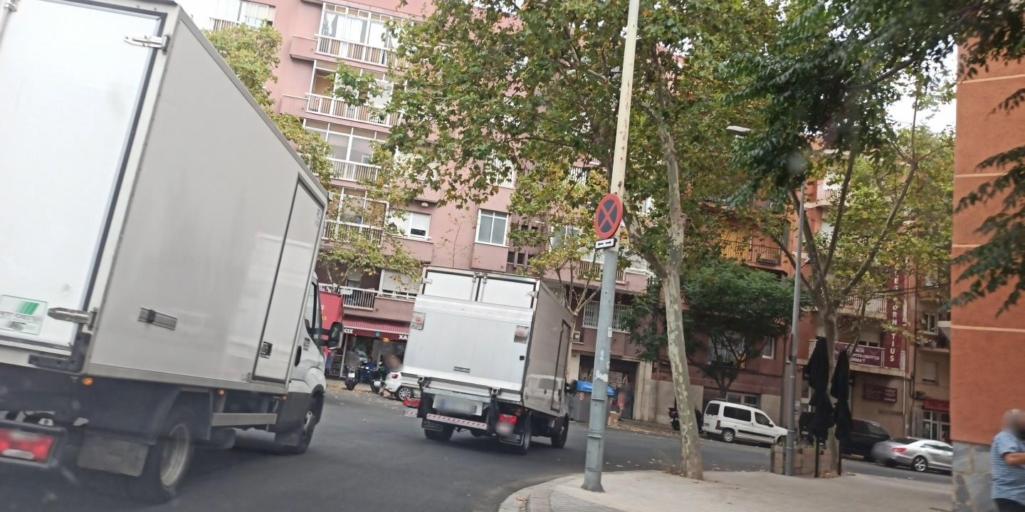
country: ES
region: Catalonia
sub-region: Provincia de Barcelona
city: Nou Barris
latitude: 41.4284
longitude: 2.1765
